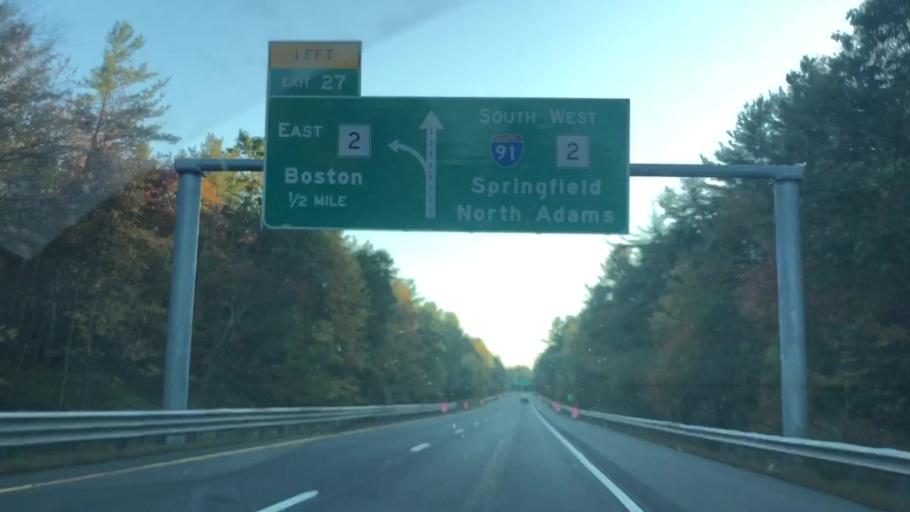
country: US
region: Massachusetts
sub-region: Franklin County
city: Turners Falls
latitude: 42.6258
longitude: -72.5861
